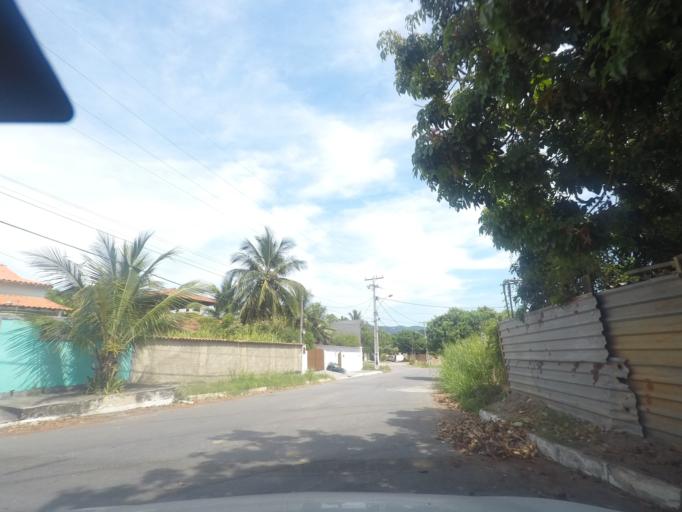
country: BR
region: Rio de Janeiro
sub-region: Marica
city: Marica
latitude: -22.9530
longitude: -42.7498
